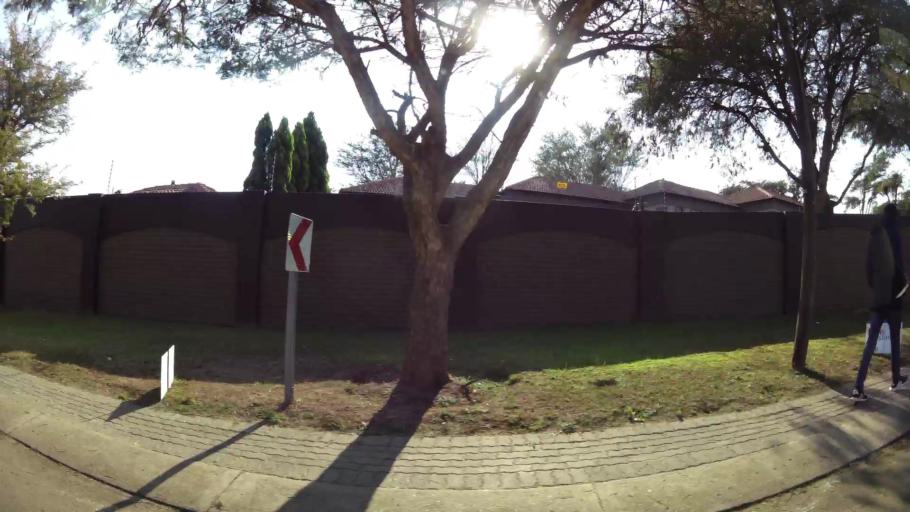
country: ZA
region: Gauteng
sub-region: City of Tshwane Metropolitan Municipality
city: Pretoria
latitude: -25.7547
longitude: 28.3346
